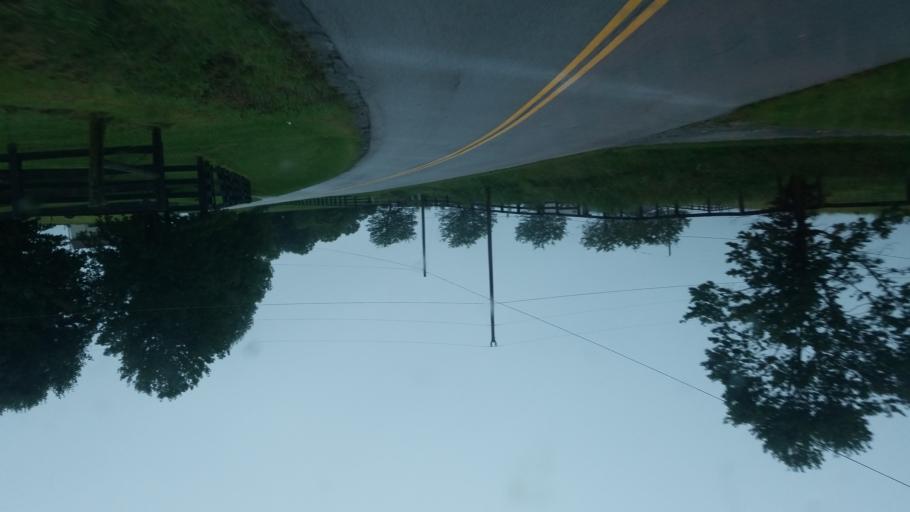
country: US
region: Kentucky
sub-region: Fleming County
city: Flemingsburg
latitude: 38.4256
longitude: -83.7152
